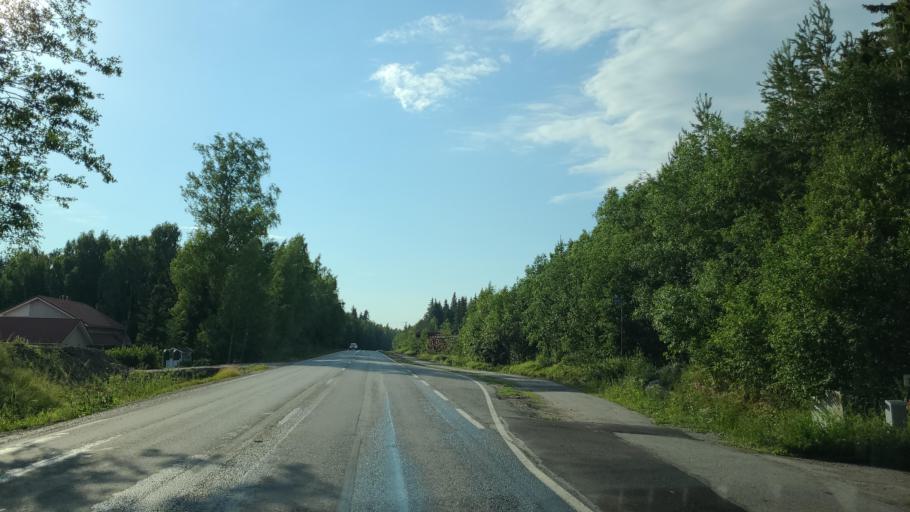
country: FI
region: Ostrobothnia
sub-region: Vaasa
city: Vaasa
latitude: 63.1980
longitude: 21.5406
